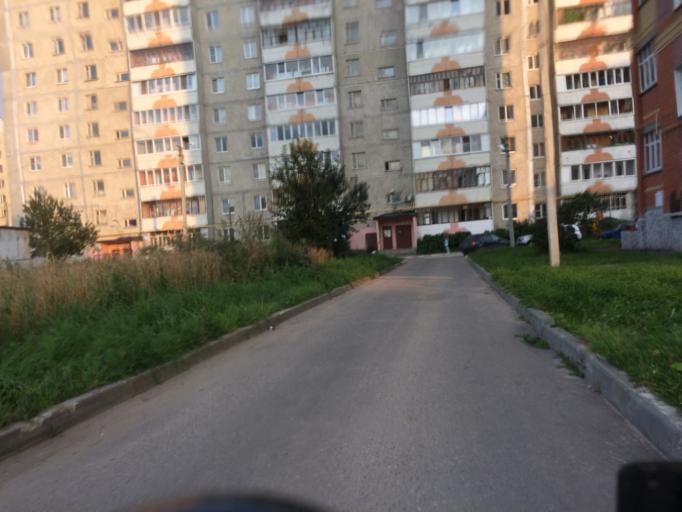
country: RU
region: Mariy-El
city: Yoshkar-Ola
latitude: 56.6435
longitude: 47.8504
